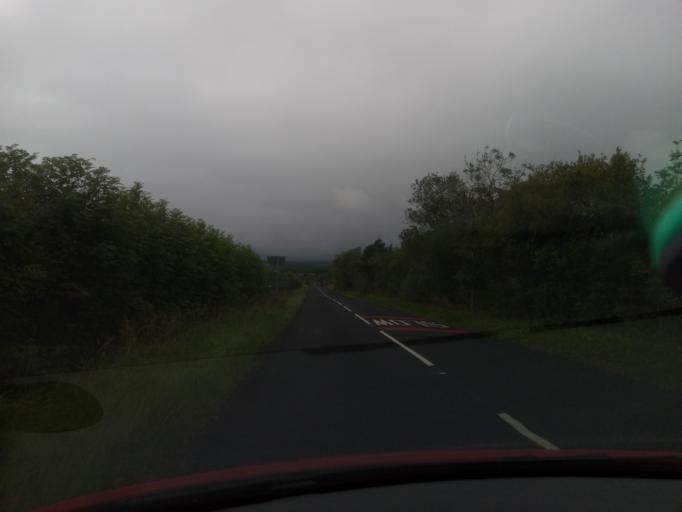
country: GB
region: England
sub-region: Northumberland
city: Rothley
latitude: 55.2014
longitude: -1.9356
